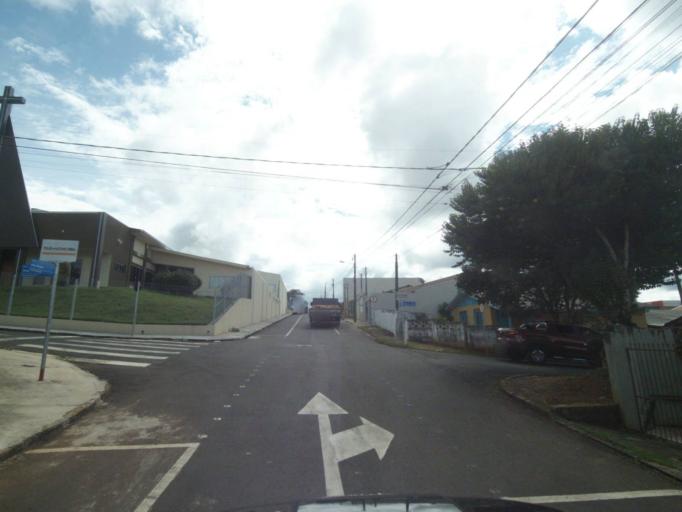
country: BR
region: Parana
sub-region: Telemaco Borba
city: Telemaco Borba
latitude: -24.3225
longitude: -50.6316
